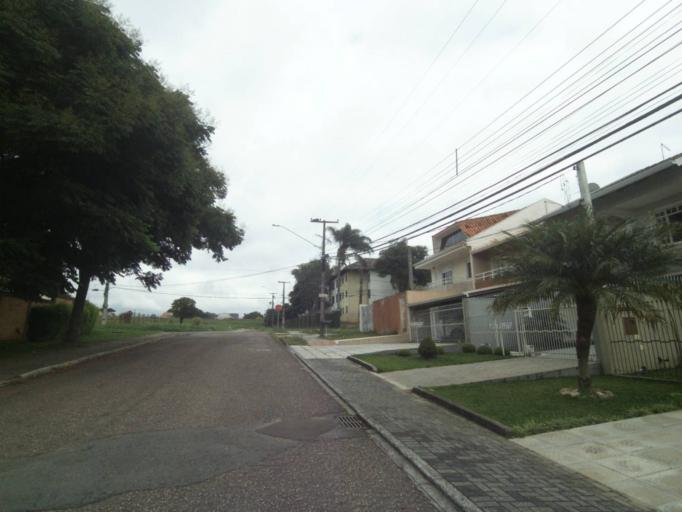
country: BR
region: Parana
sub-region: Pinhais
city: Pinhais
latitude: -25.4578
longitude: -49.2199
